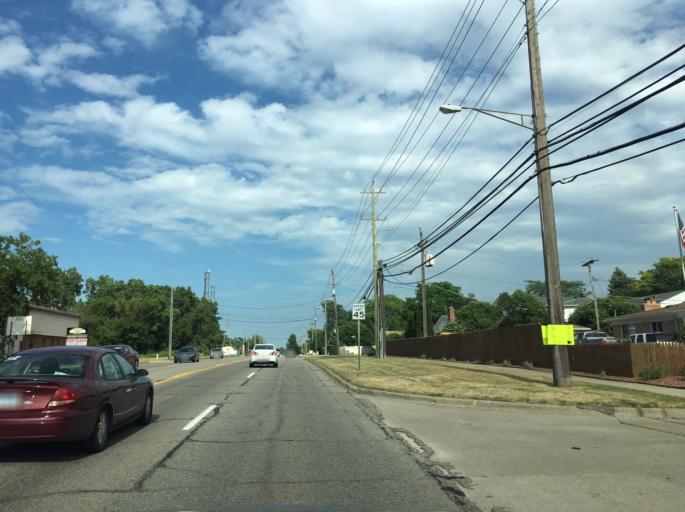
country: US
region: Michigan
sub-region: Macomb County
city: Sterling Heights
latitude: 42.5375
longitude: -83.0022
